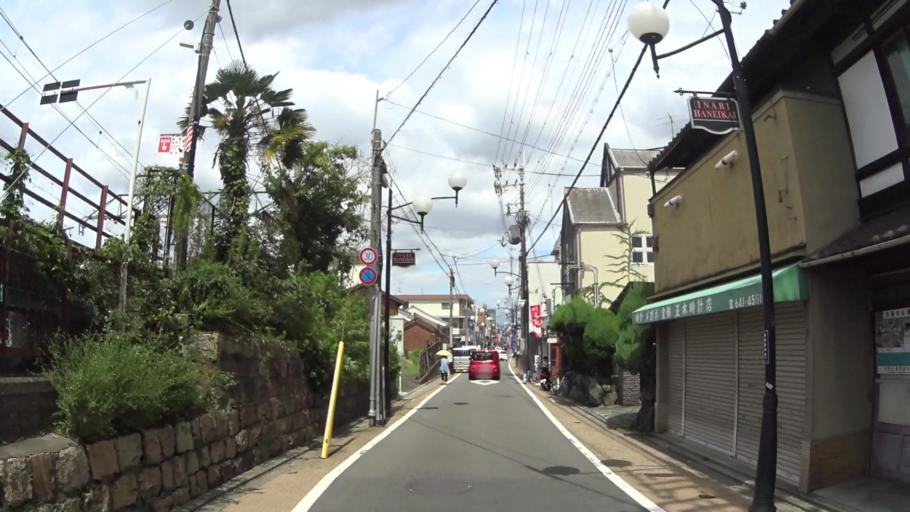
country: JP
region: Kyoto
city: Kyoto
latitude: 34.9661
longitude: 135.7711
